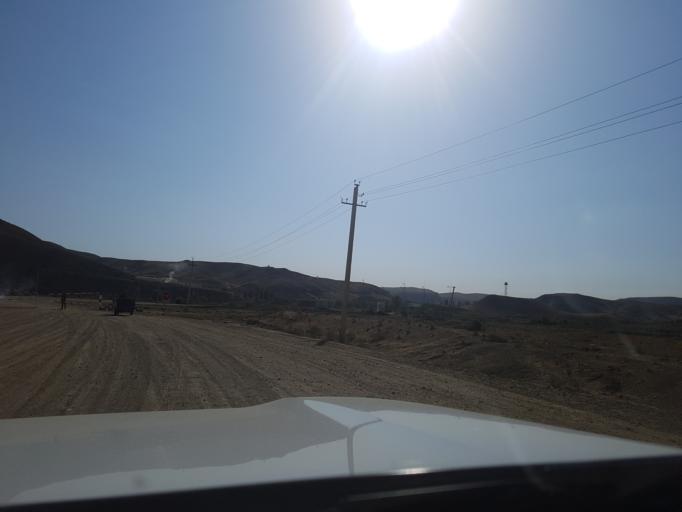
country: TM
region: Balkan
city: Magtymguly
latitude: 38.2923
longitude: 56.7431
